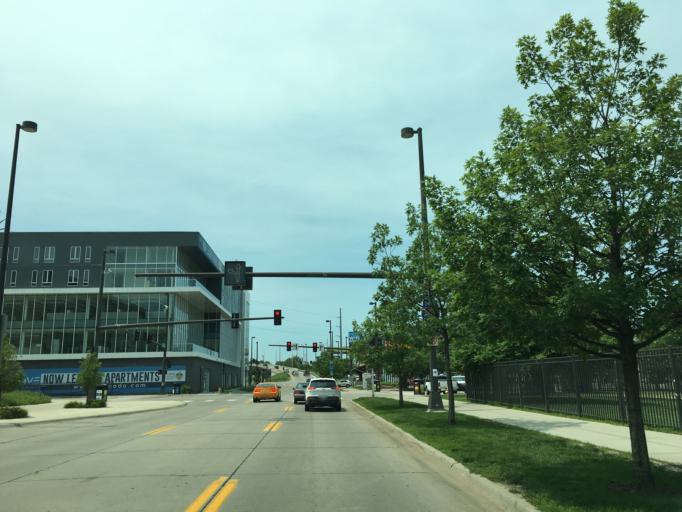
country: US
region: Nebraska
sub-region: Douglas County
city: Omaha
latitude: 41.2637
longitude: -95.9310
